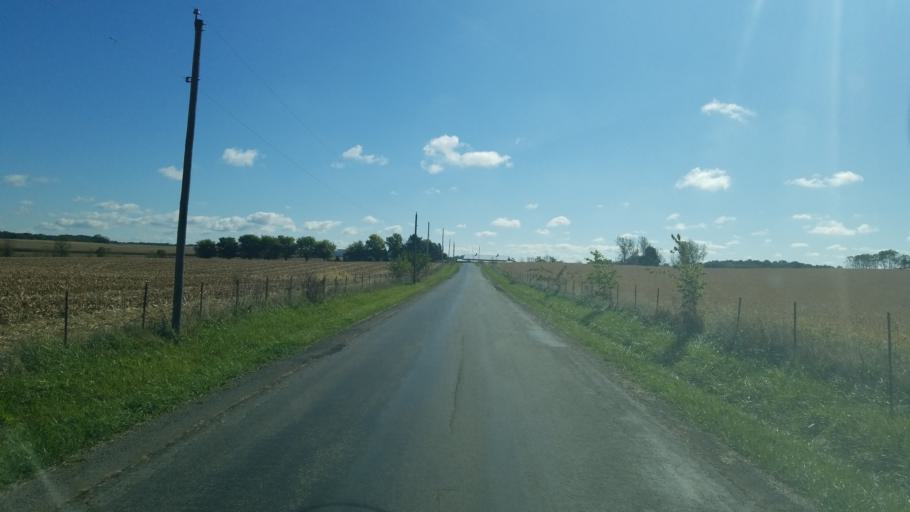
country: US
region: Ohio
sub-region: Highland County
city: Leesburg
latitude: 39.2791
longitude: -83.5702
